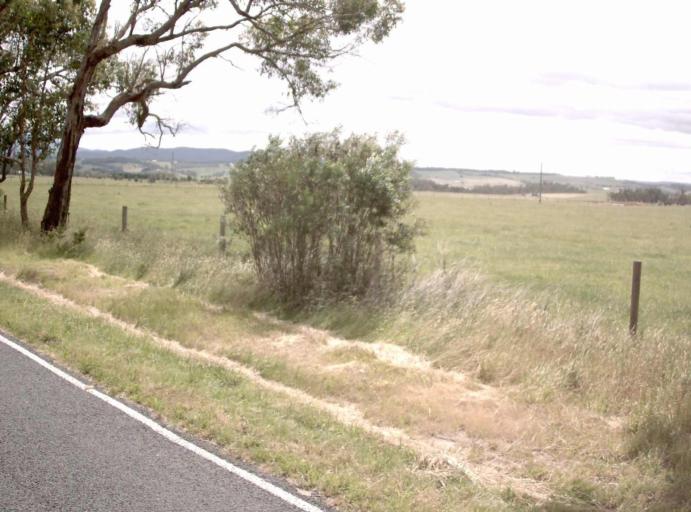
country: AU
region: Victoria
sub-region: Latrobe
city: Moe
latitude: -38.1178
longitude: 146.1490
